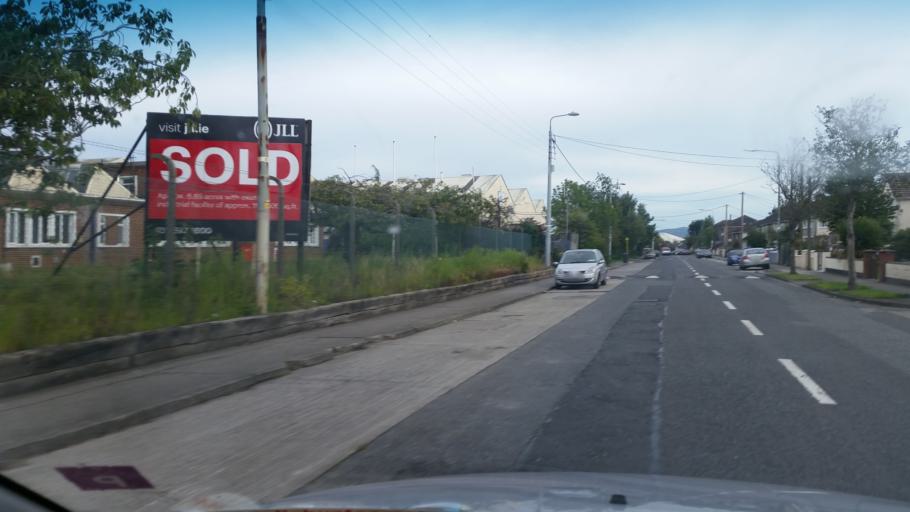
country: IE
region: Leinster
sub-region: Dublin City
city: Finglas
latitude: 53.3951
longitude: -6.3015
